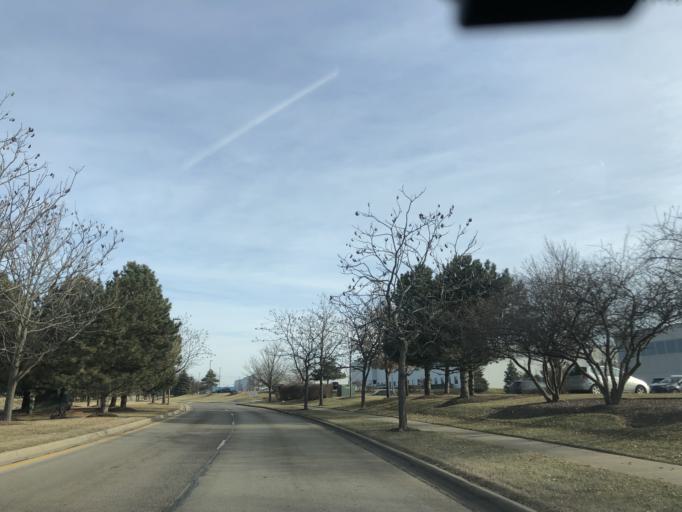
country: US
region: Illinois
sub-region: Cook County
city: Lemont
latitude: 41.6962
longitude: -88.0172
